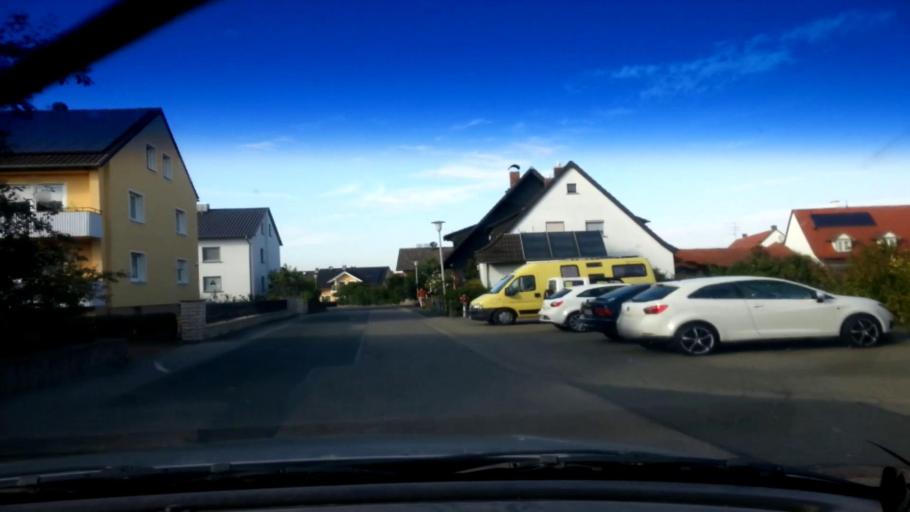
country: DE
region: Bavaria
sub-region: Upper Franconia
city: Breitengussbach
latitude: 49.9688
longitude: 10.8834
